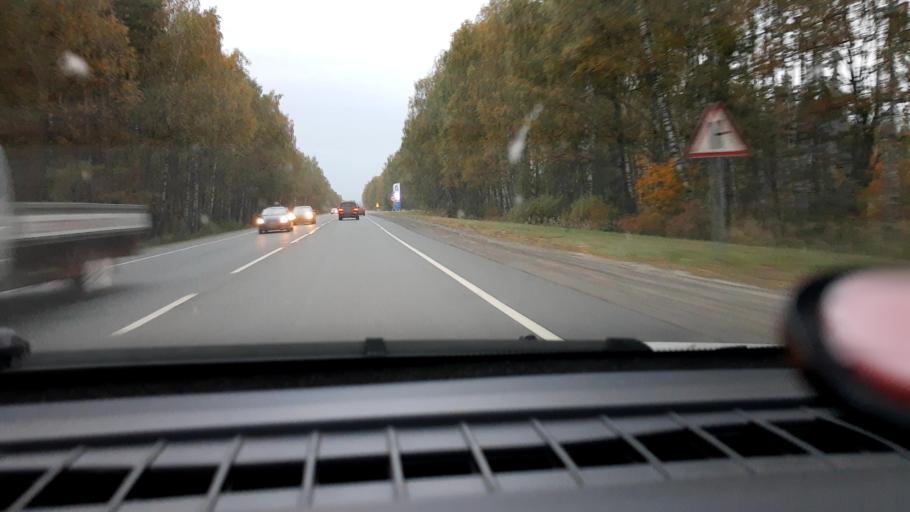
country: RU
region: Vladimir
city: Orgtrud
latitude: 56.2100
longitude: 40.6161
